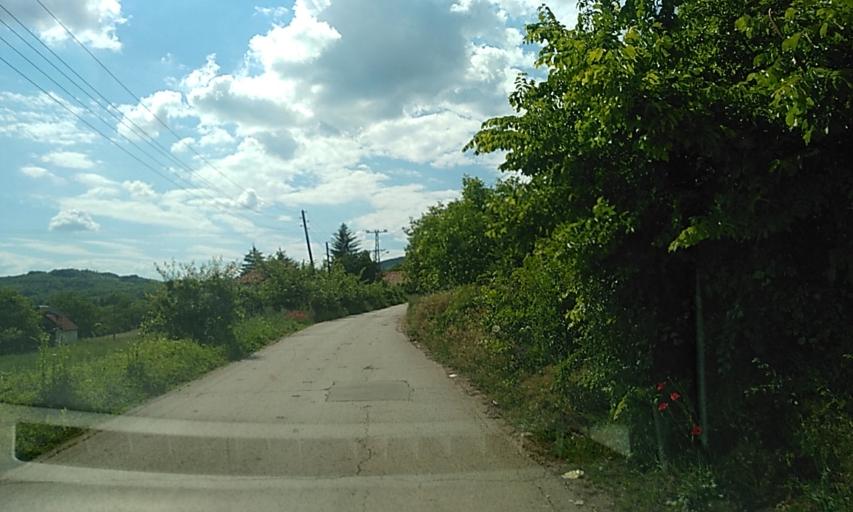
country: RS
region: Central Serbia
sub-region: Nisavski Okrug
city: Niska Banja
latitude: 43.3610
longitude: 22.0371
